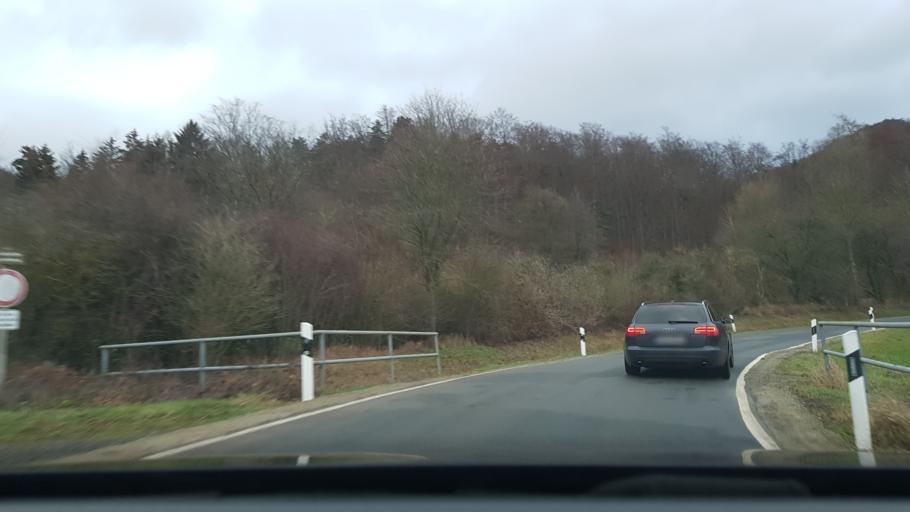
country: DE
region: Lower Saxony
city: Juhnde
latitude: 51.3998
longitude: 9.7855
